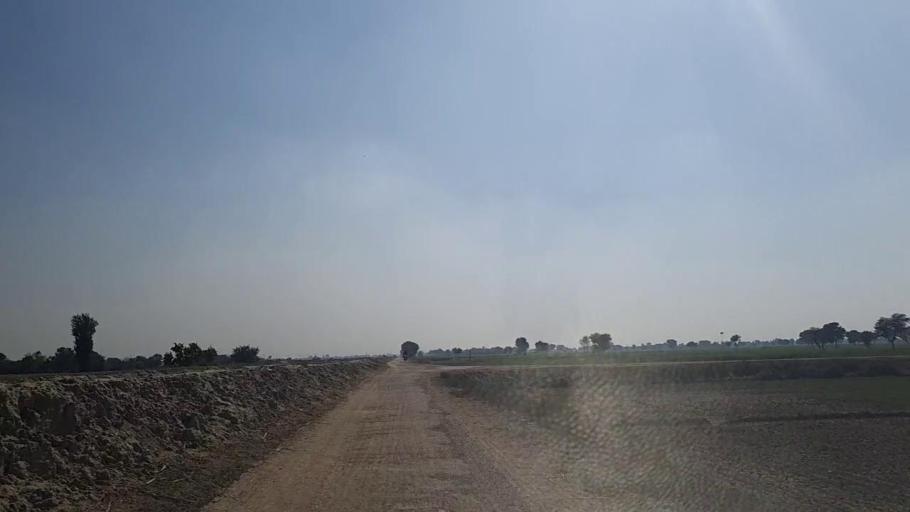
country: PK
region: Sindh
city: Shahpur Chakar
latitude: 26.2149
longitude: 68.5839
